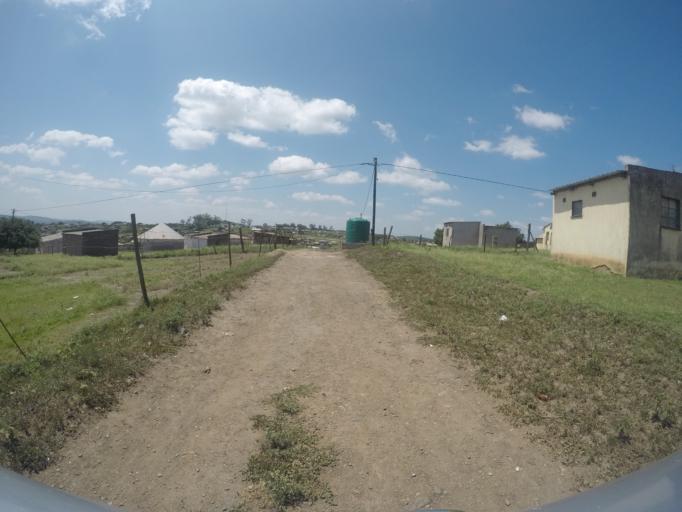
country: ZA
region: KwaZulu-Natal
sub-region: uThungulu District Municipality
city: Empangeni
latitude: -28.6077
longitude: 31.7380
